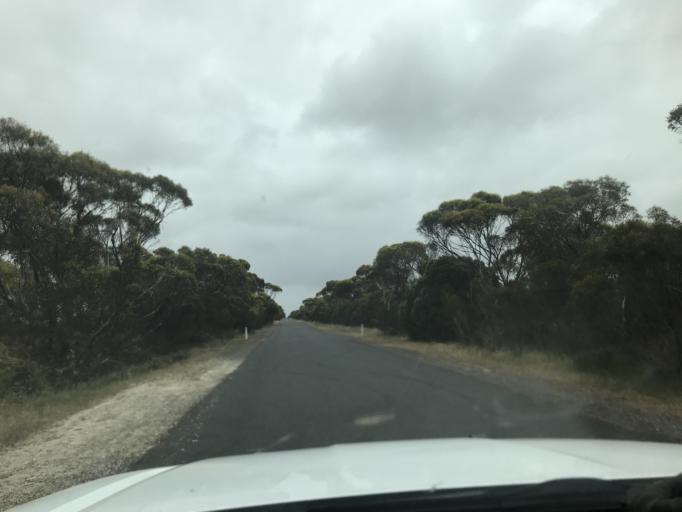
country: AU
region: South Australia
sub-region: Tatiara
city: Bordertown
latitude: -36.1205
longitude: 141.0638
